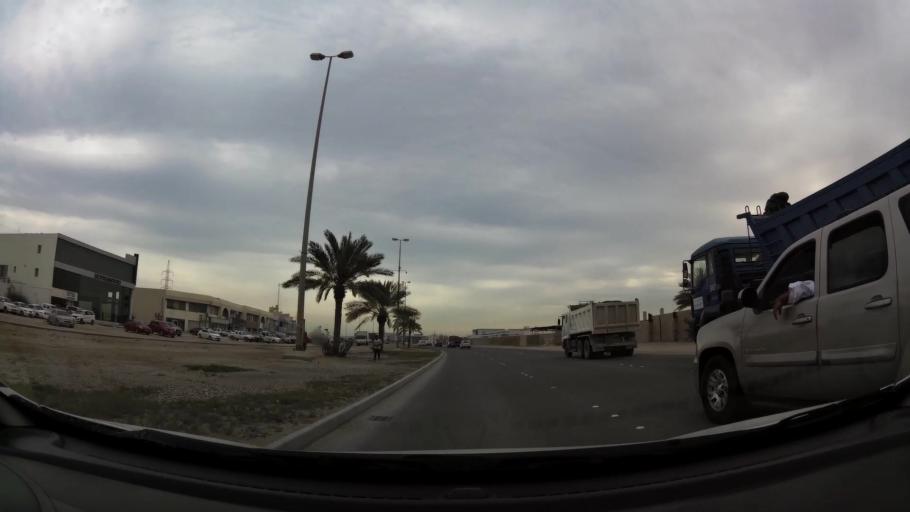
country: BH
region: Northern
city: Sitrah
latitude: 26.1584
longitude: 50.6058
